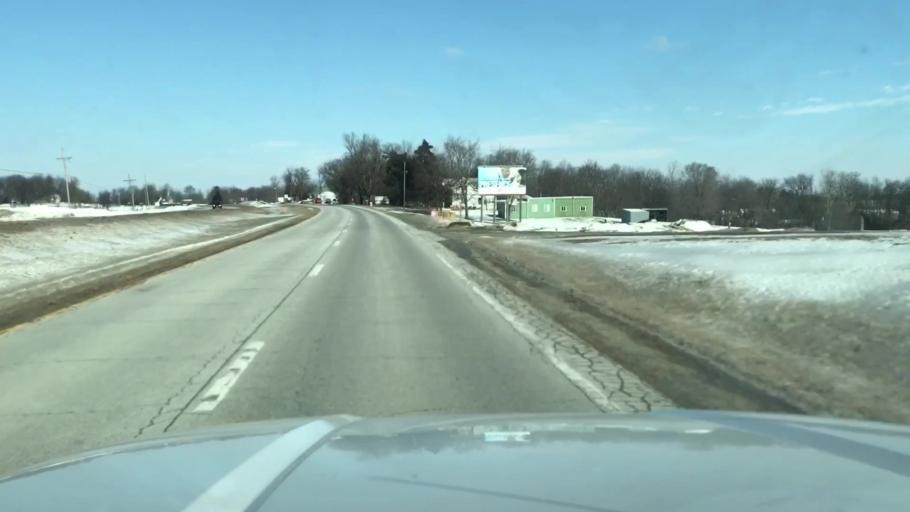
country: US
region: Missouri
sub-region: Andrew County
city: Savannah
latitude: 39.9066
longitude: -94.8094
